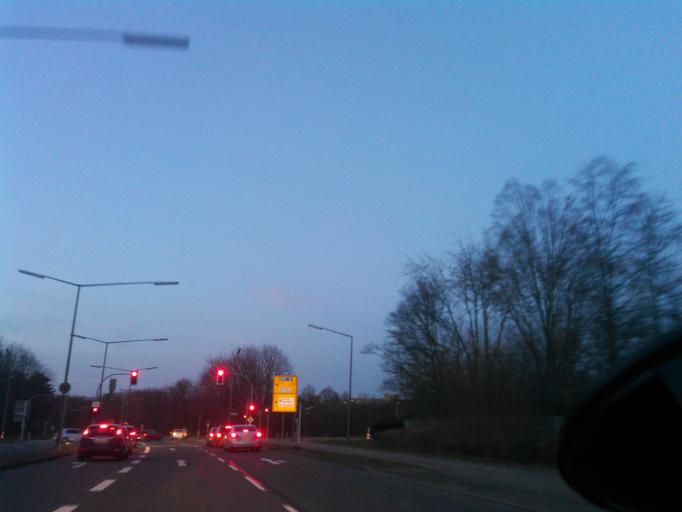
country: DE
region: North Rhine-Westphalia
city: Marl
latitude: 51.6483
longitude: 7.1039
